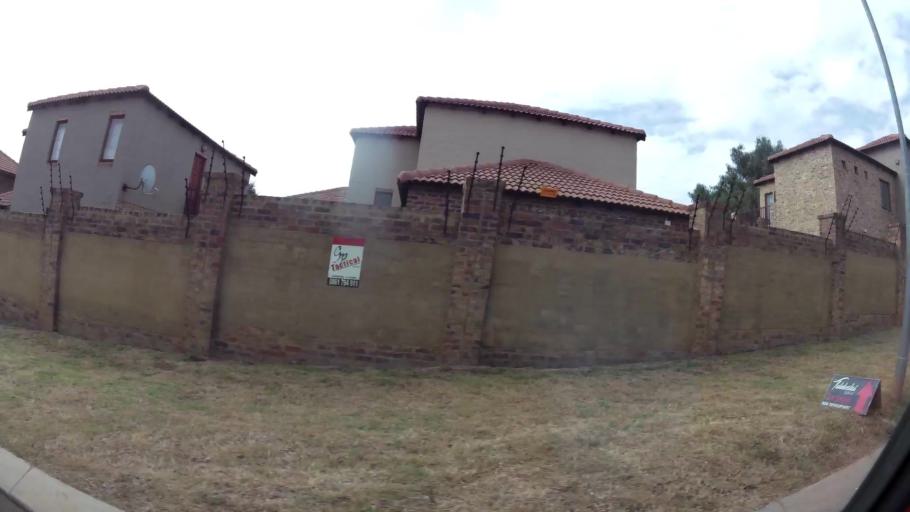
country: ZA
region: Gauteng
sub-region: City of Johannesburg Metropolitan Municipality
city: Roodepoort
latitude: -26.1000
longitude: 27.8798
